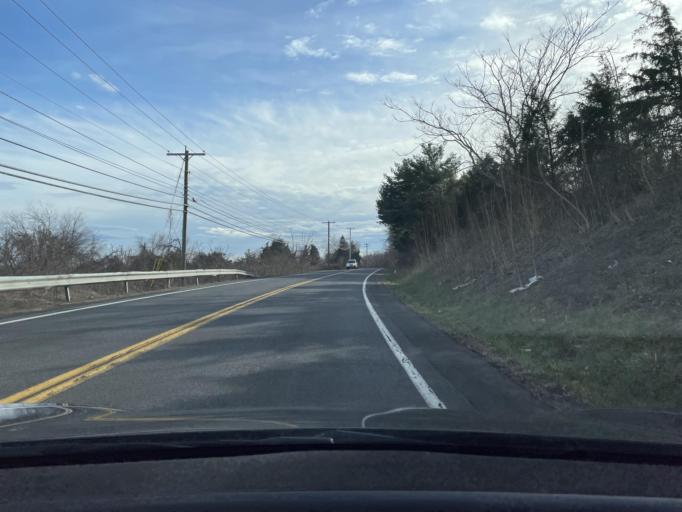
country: US
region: New York
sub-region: Ulster County
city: Lincoln Park
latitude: 41.9571
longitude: -74.0176
